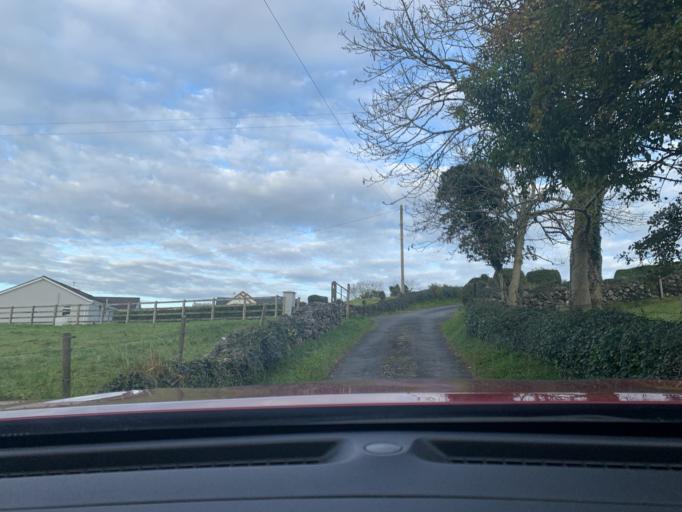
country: IE
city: Ballisodare
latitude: 54.2301
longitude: -8.5114
